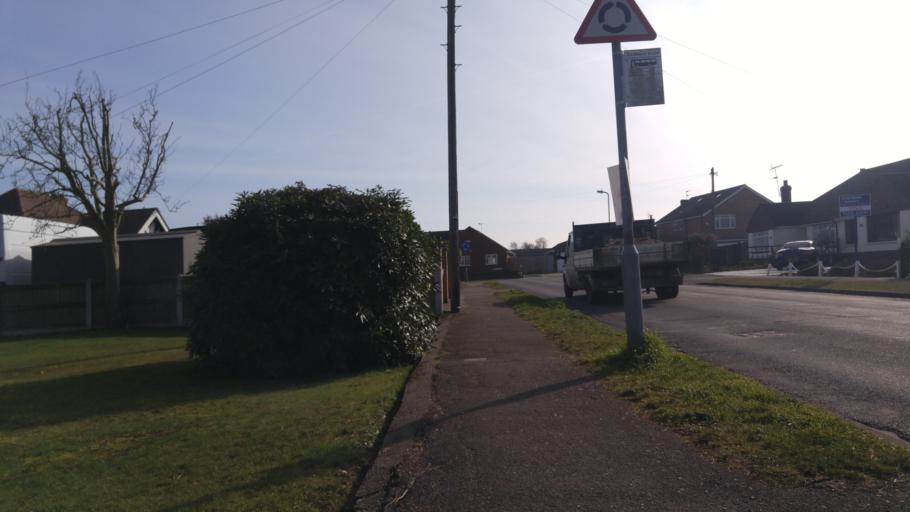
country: GB
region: England
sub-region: Essex
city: Clacton-on-Sea
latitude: 51.8104
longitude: 1.1668
